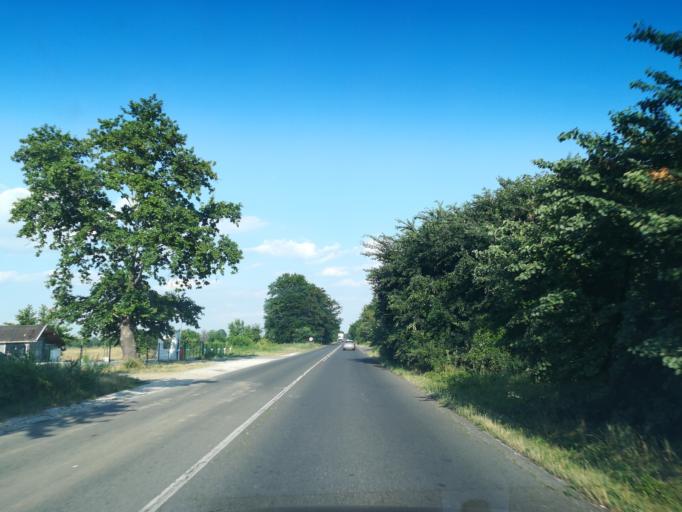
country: BG
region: Plovdiv
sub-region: Obshtina Plovdiv
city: Plovdiv
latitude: 42.1483
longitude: 24.8338
